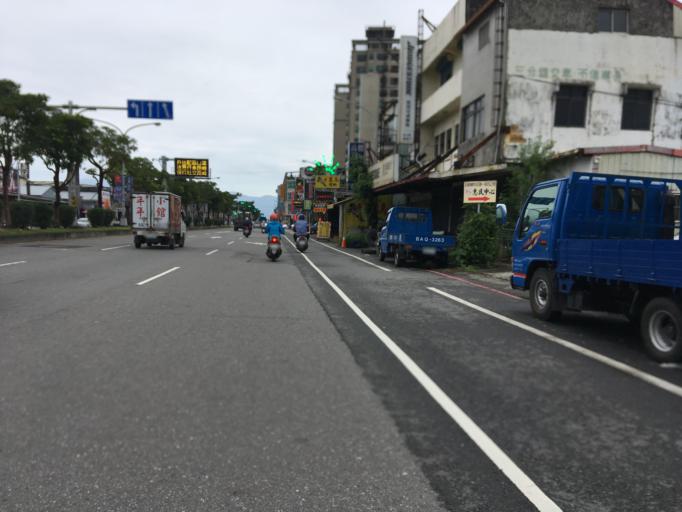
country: TW
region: Taiwan
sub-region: Yilan
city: Yilan
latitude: 24.6888
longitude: 121.7706
